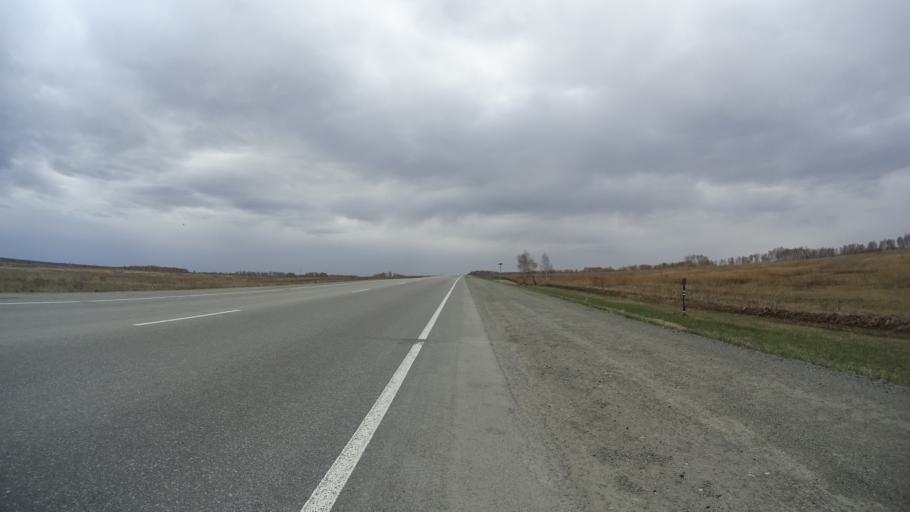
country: RU
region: Chelyabinsk
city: Yemanzhelinsk
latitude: 54.7073
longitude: 61.2576
